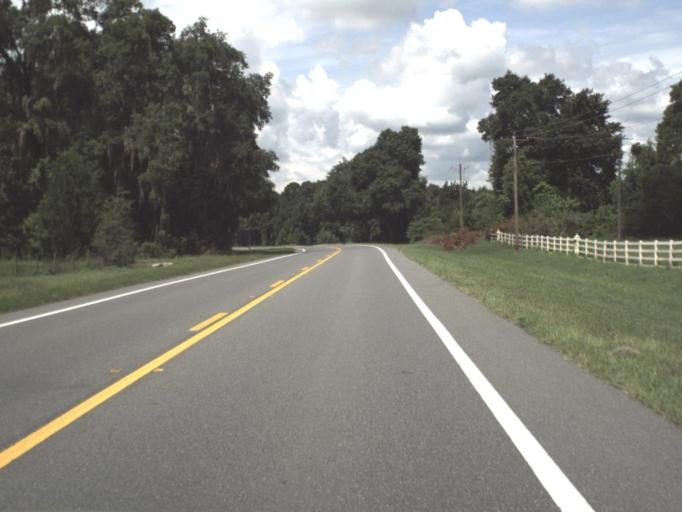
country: US
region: Florida
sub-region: Alachua County
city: Alachua
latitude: 29.8122
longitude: -82.4672
